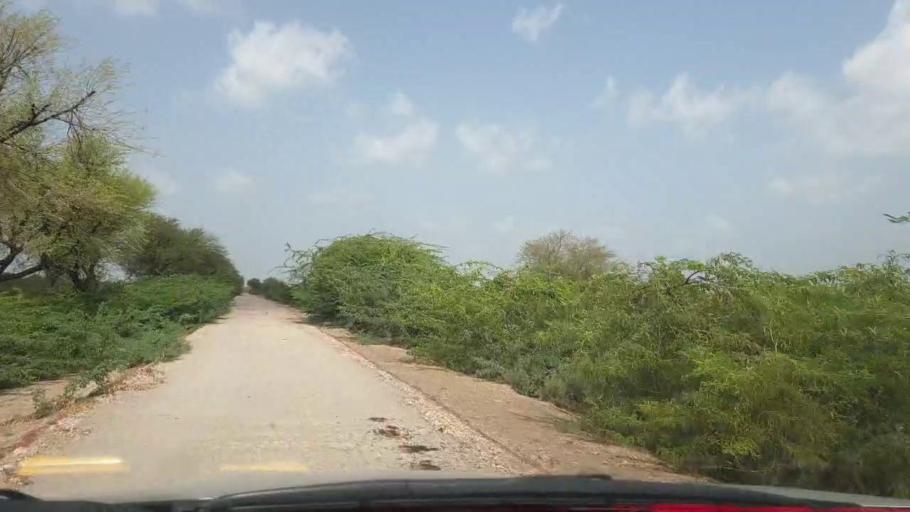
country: PK
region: Sindh
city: Rajo Khanani
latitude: 24.9157
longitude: 68.8980
